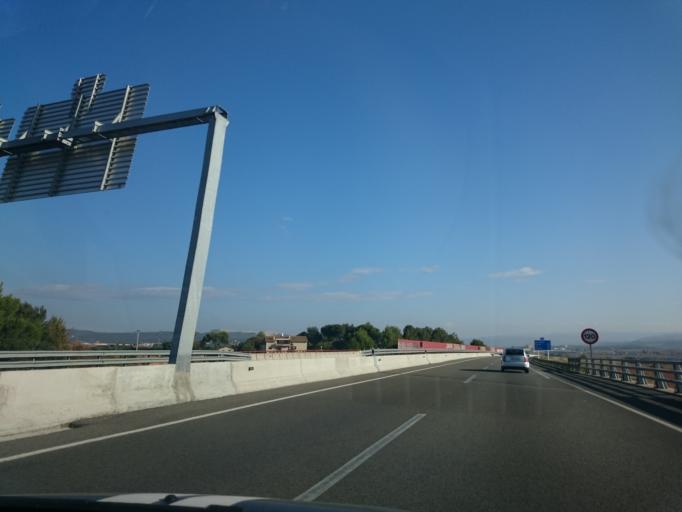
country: ES
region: Catalonia
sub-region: Provincia de Barcelona
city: Sant Fruitos de Bages
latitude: 41.7532
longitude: 1.8458
